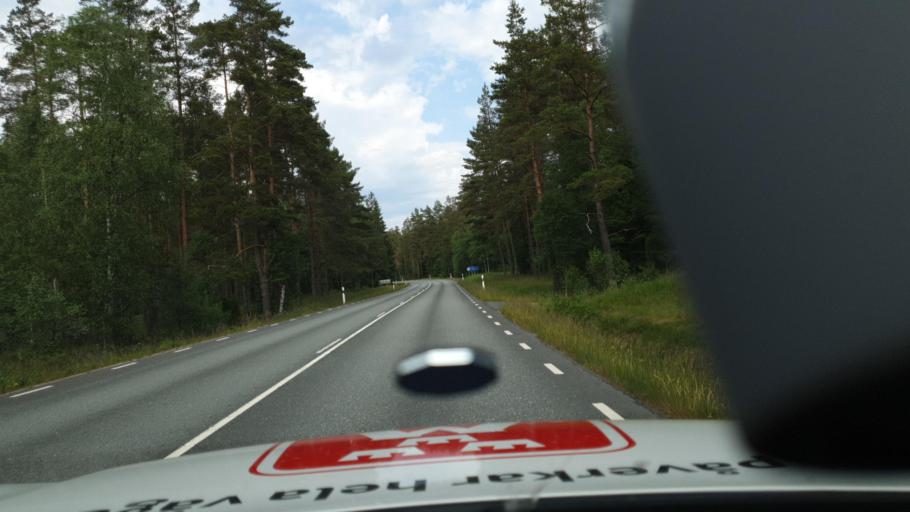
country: SE
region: Joenkoeping
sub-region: Vaggeryds Kommun
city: Skillingaryd
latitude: 57.3207
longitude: 14.0953
